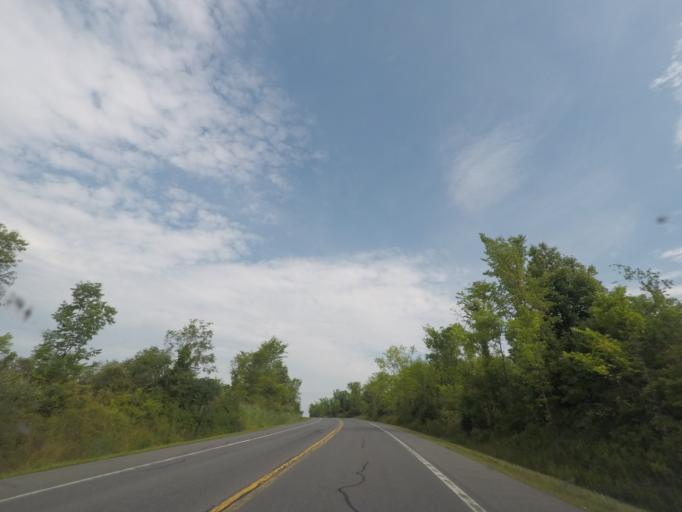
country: US
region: New York
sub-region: Rensselaer County
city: Poestenkill
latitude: 42.6985
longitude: -73.5600
